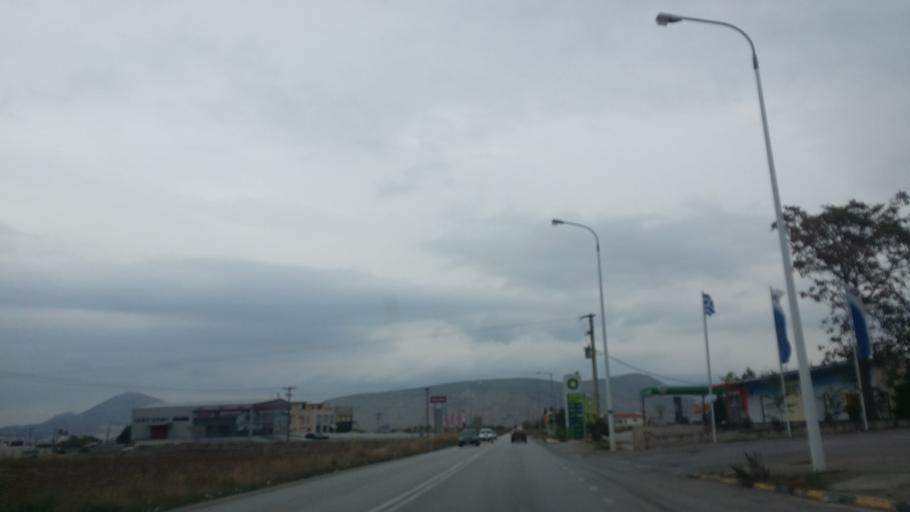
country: GR
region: Central Greece
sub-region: Nomos Voiotias
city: Thivai
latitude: 38.3459
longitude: 23.3223
